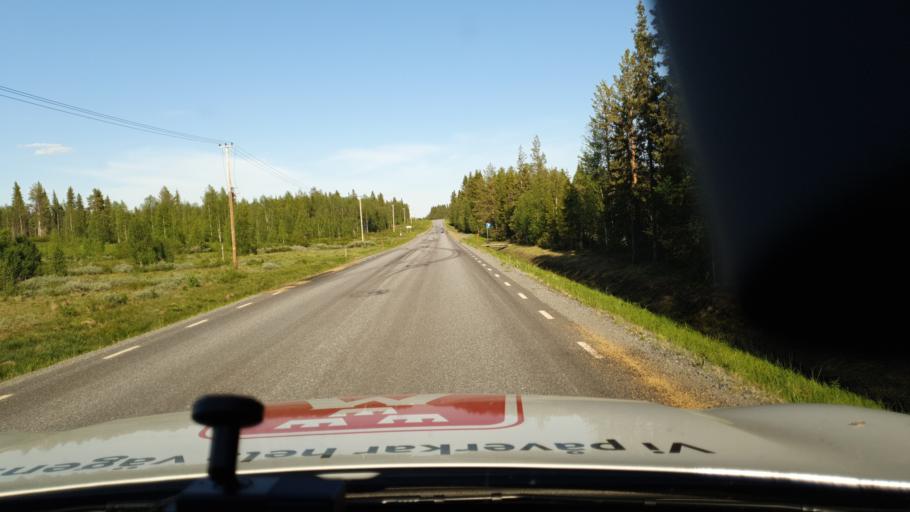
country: SE
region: Vaesterbotten
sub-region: Storumans Kommun
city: Storuman
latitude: 64.7038
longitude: 17.1474
